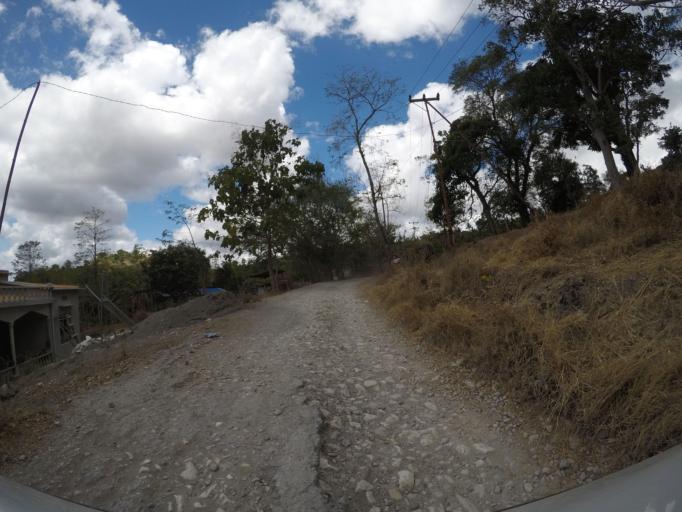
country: TL
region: Baucau
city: Baucau
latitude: -8.5112
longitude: 126.6806
